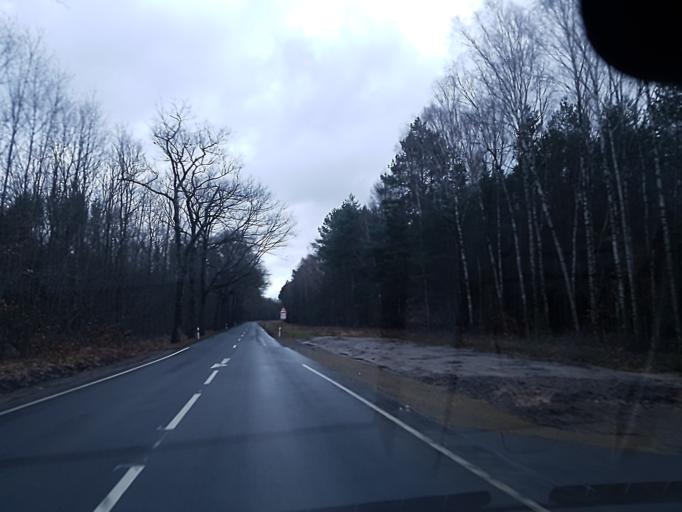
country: DE
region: Brandenburg
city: Hohenleipisch
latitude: 51.5242
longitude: 13.5789
